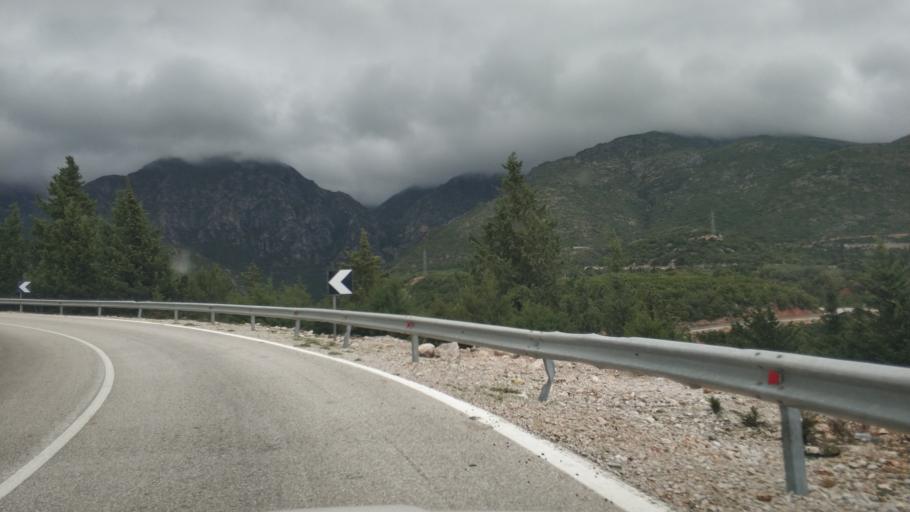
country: AL
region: Vlore
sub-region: Rrethi i Vlores
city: Vranisht
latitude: 40.1403
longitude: 19.6752
